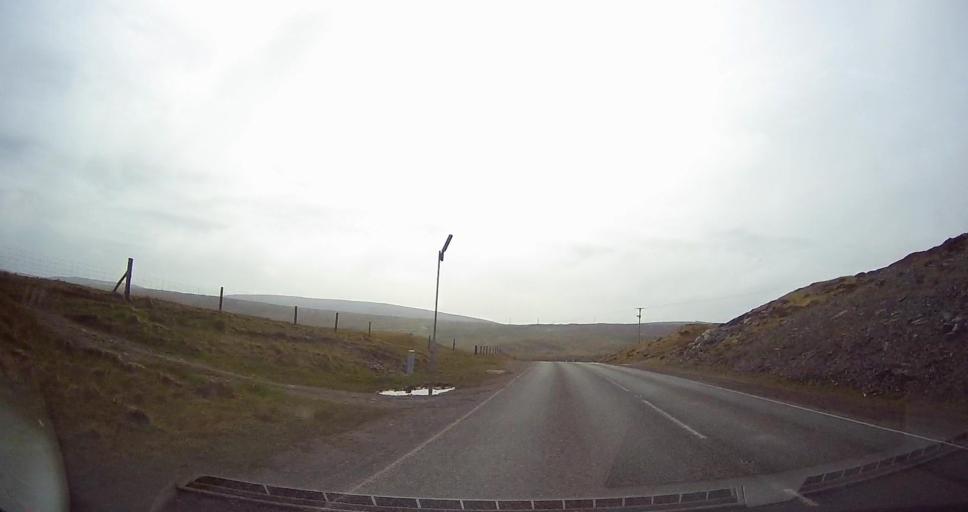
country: GB
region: Scotland
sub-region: Shetland Islands
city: Lerwick
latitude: 60.1392
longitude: -1.2034
